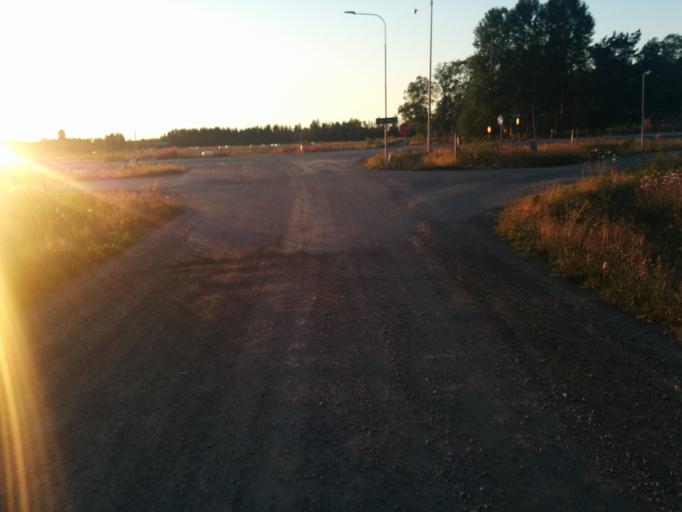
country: SE
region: Vaesterbotten
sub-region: Umea Kommun
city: Ersmark
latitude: 63.8552
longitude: 20.3881
